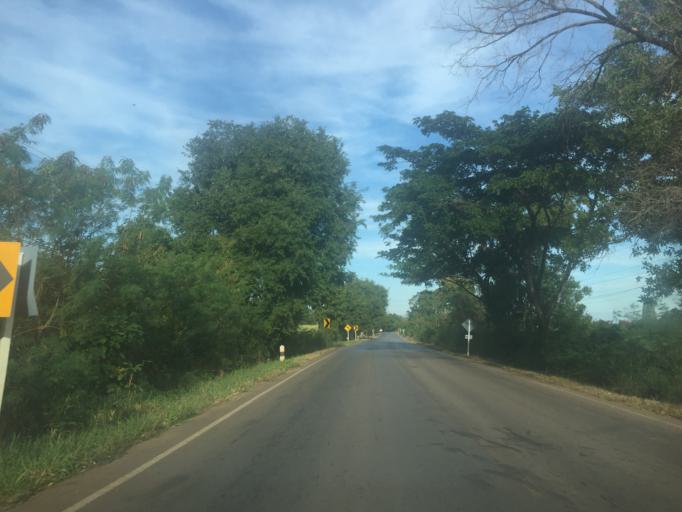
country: TH
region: Changwat Udon Thani
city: Si That
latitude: 16.9856
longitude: 103.1785
